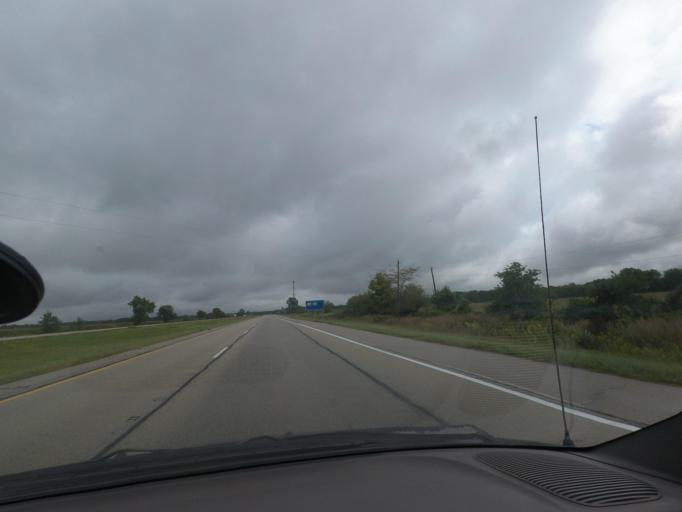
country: US
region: Illinois
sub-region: Piatt County
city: Monticello
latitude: 40.0391
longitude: -88.5910
